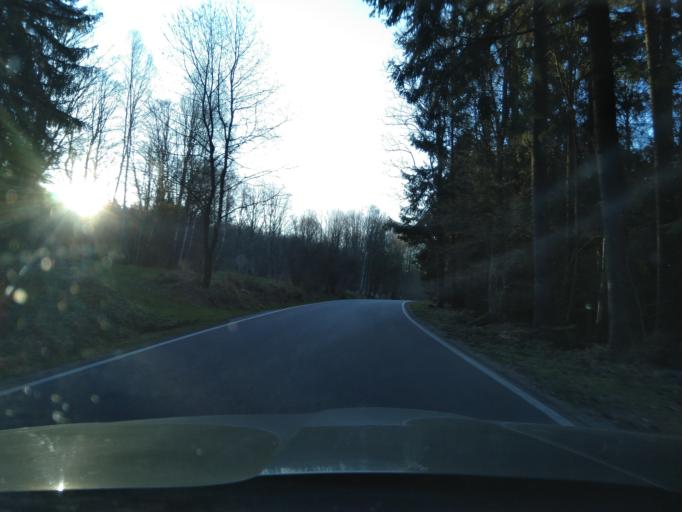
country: CZ
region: Jihocesky
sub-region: Okres Prachatice
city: Vimperk
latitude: 48.9552
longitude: 13.7732
